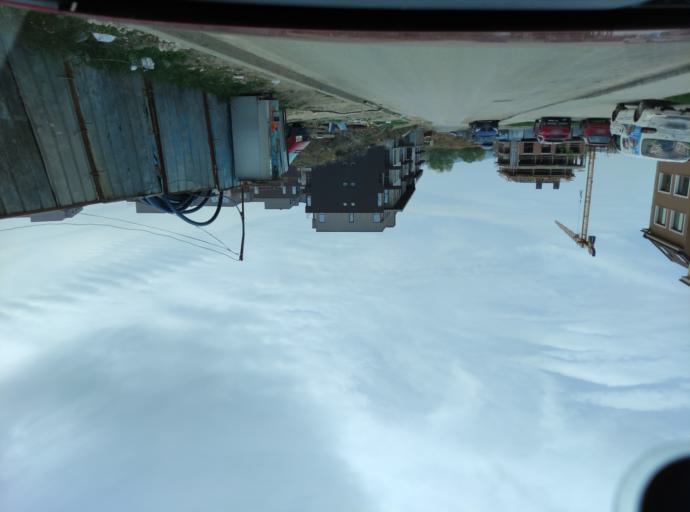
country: BG
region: Sofia-Capital
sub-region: Stolichna Obshtina
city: Sofia
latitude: 42.6361
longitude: 23.3417
